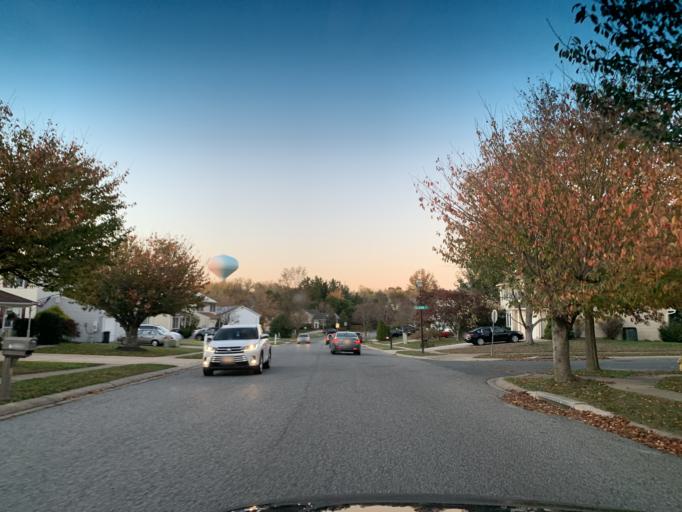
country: US
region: Maryland
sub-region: Harford County
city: South Bel Air
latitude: 39.5352
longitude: -76.3037
